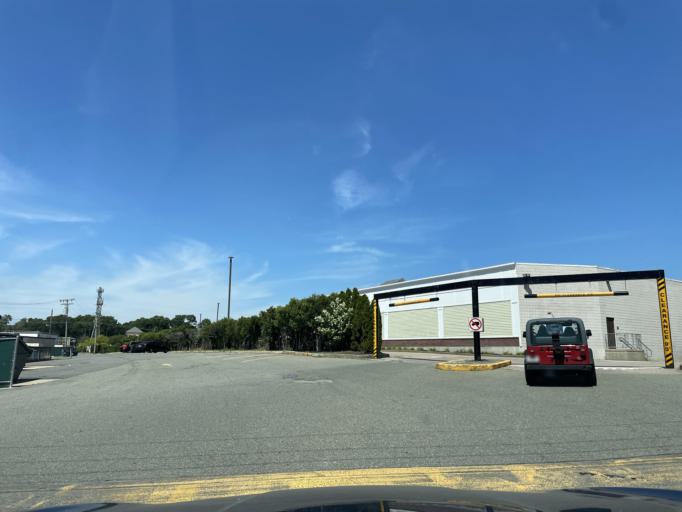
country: US
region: Massachusetts
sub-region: Norfolk County
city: Canton
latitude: 42.1381
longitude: -71.1471
